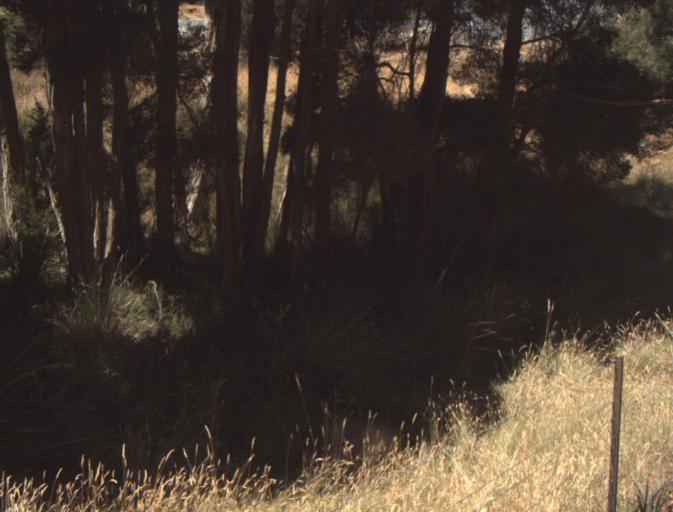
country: AU
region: Tasmania
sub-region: Launceston
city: Newstead
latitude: -41.3504
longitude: 147.3776
